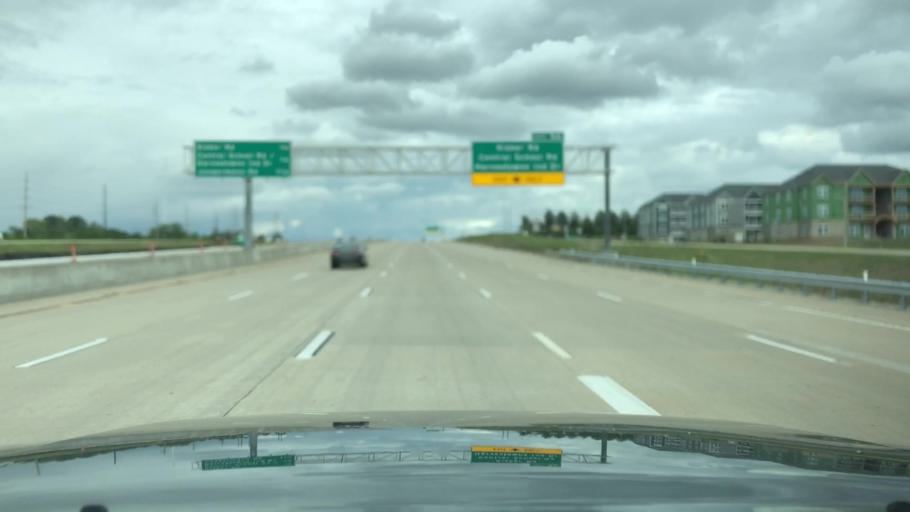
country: US
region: Missouri
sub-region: Saint Charles County
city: Cottleville
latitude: 38.7387
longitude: -90.6283
